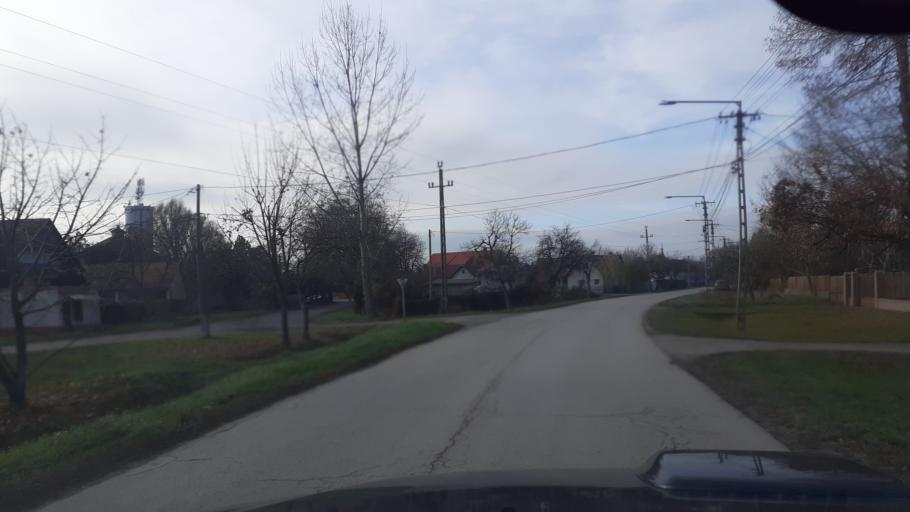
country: HU
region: Pest
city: Domsod
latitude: 47.0930
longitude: 19.0130
